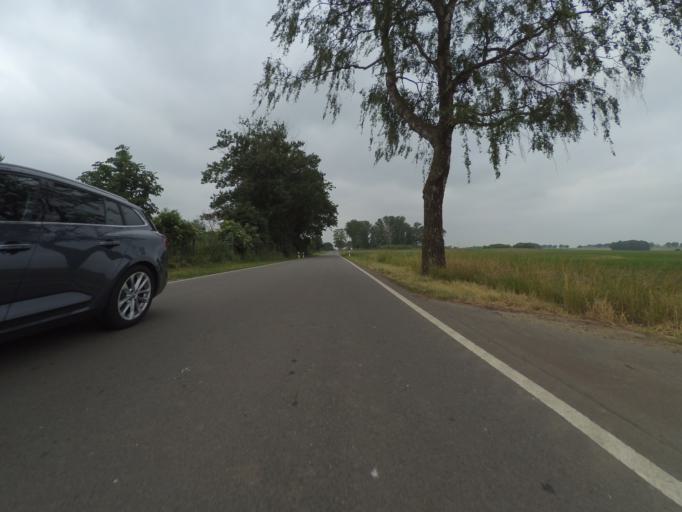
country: DE
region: Mecklenburg-Vorpommern
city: Domsuhl
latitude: 53.4884
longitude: 11.7326
